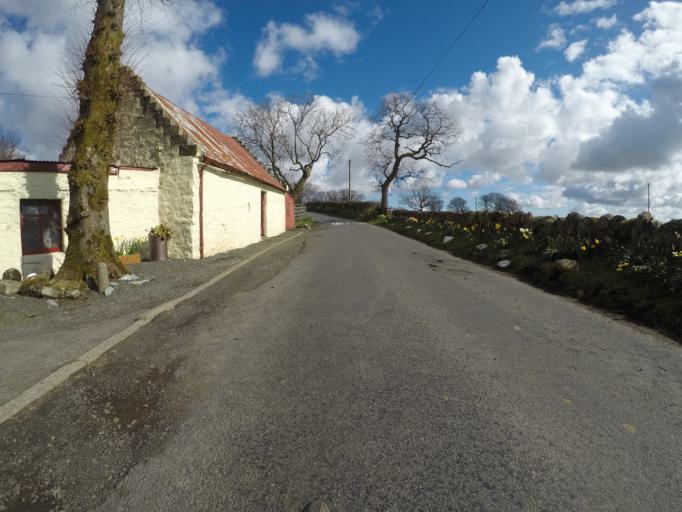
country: GB
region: Scotland
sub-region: North Ayrshire
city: Beith
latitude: 55.7200
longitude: -4.6185
